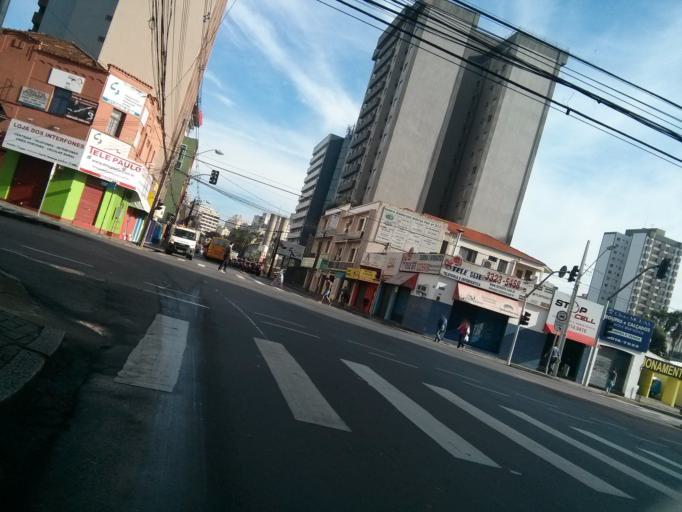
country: BR
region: Parana
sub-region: Curitiba
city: Curitiba
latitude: -25.4399
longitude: -49.2720
